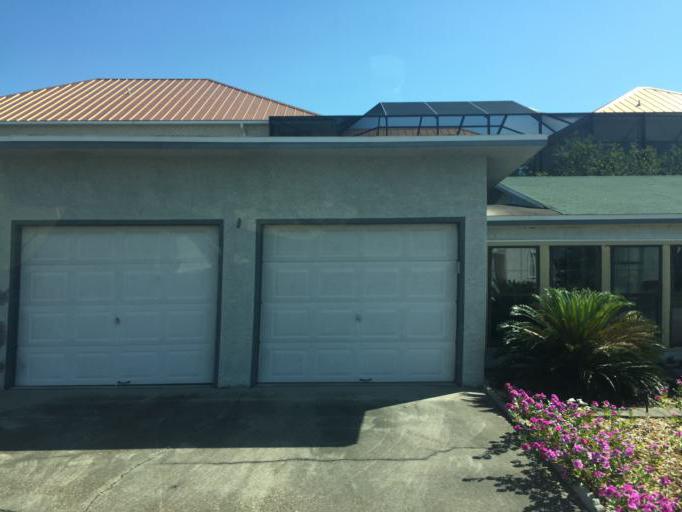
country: US
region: Florida
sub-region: Bay County
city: Panama City Beach
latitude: 30.2026
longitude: -85.8477
